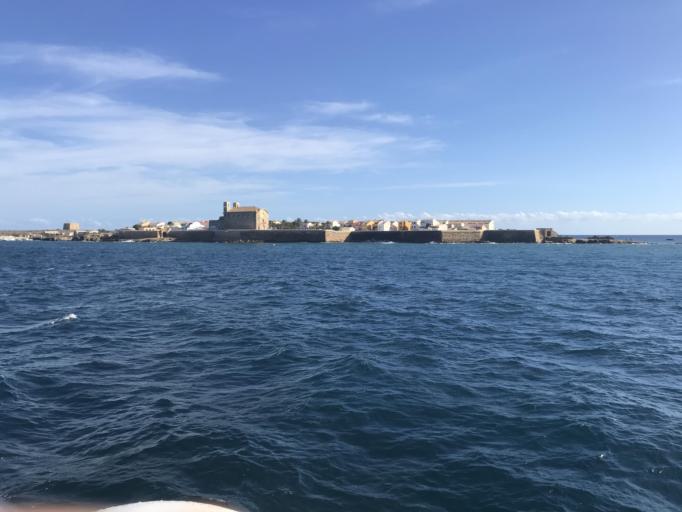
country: ES
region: Valencia
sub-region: Provincia de Alicante
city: Santa Pola
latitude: 38.1700
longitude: -0.4849
